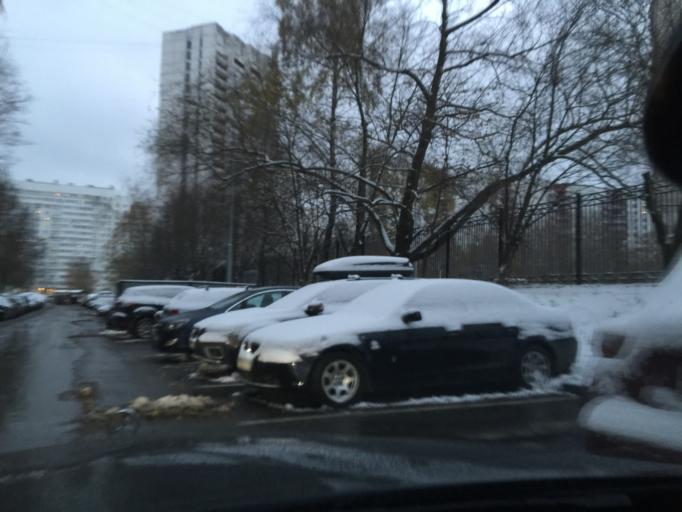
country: RU
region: Moscow
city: Troparevo
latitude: 55.6425
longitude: 37.4776
